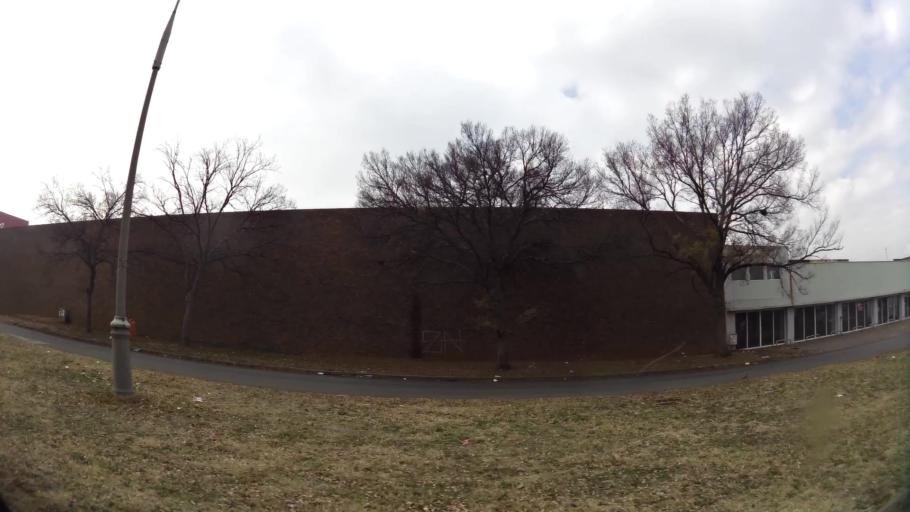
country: ZA
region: Gauteng
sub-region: Sedibeng District Municipality
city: Vanderbijlpark
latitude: -26.7044
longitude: 27.8471
